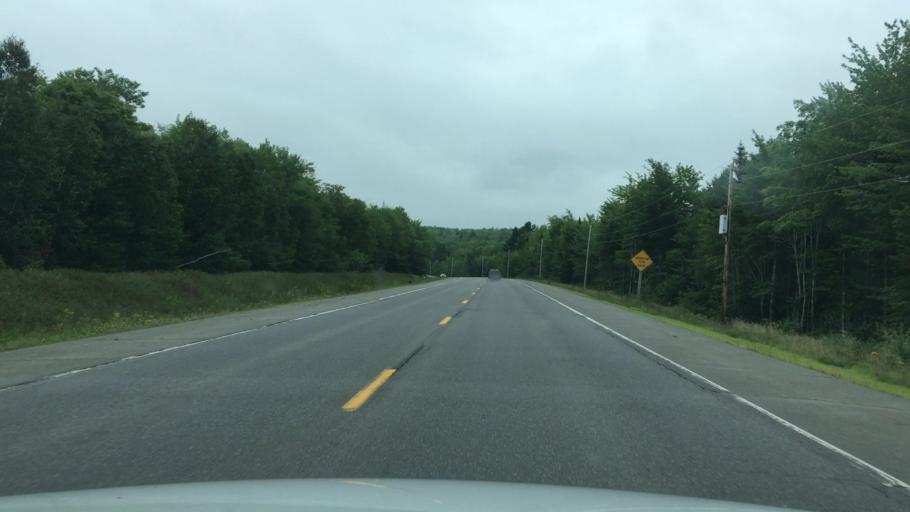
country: US
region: Maine
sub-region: Hancock County
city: Franklin
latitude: 44.8327
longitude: -68.1365
